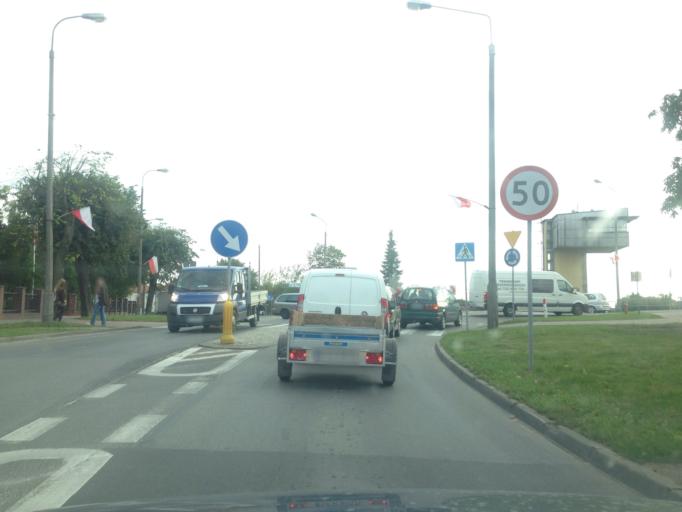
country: PL
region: Pomeranian Voivodeship
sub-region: Powiat kwidzynski
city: Kwidzyn
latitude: 53.7353
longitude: 18.9364
